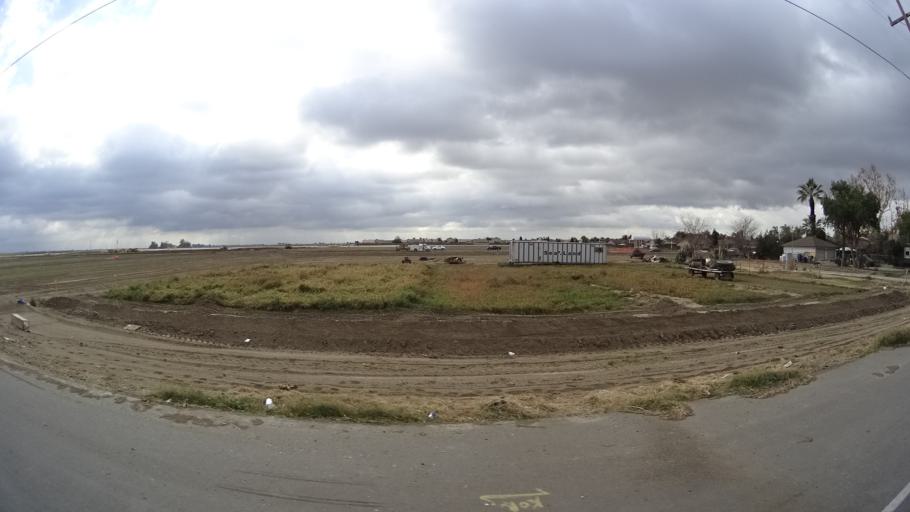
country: US
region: California
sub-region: Kern County
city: Greenfield
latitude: 35.2959
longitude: -118.9956
